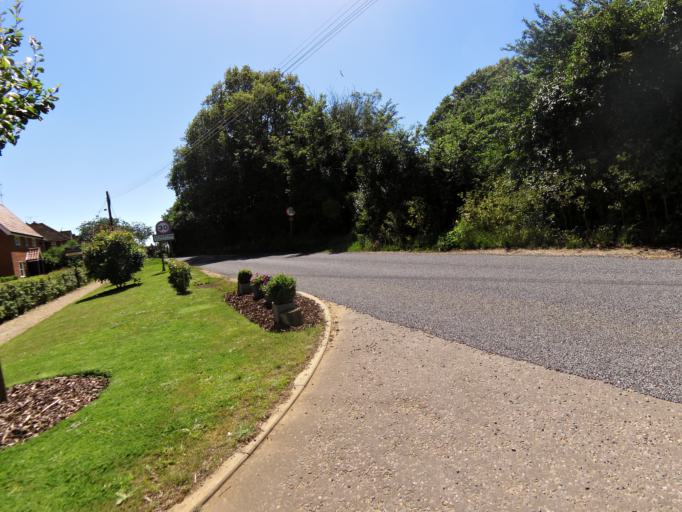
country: GB
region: England
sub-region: Suffolk
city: Felixstowe
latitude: 52.0275
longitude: 1.4163
